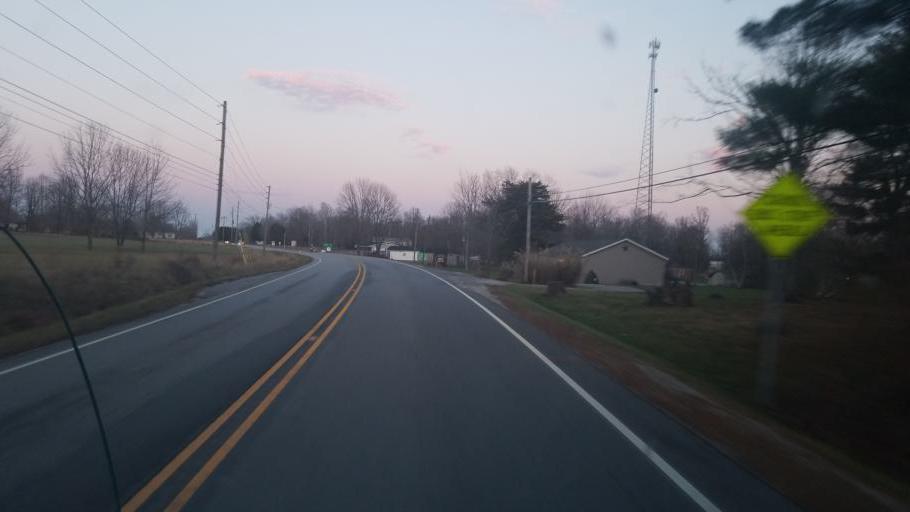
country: US
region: Indiana
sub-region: Lawrence County
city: Bedford
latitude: 38.8746
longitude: -86.2842
